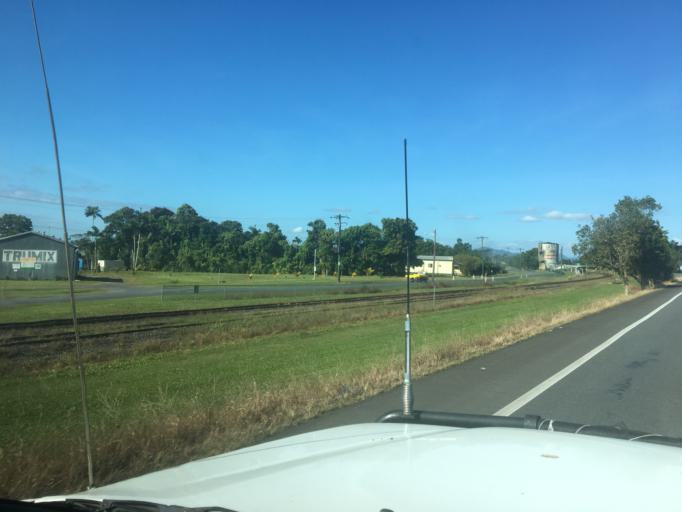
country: AU
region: Queensland
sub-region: Cassowary Coast
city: Innisfail
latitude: -17.3388
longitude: 145.9265
